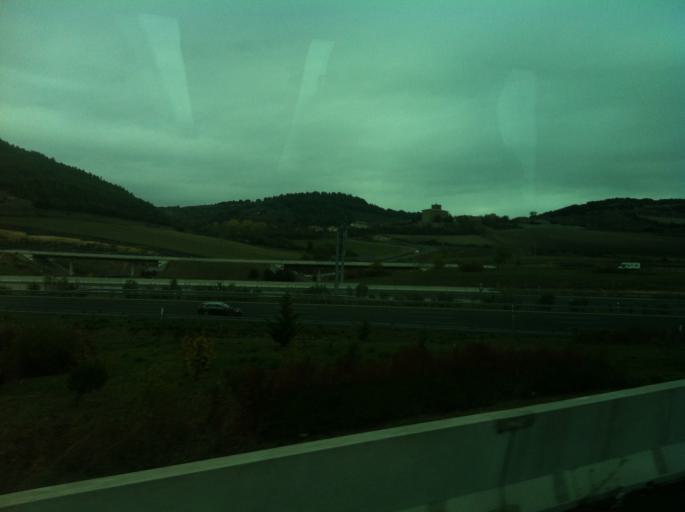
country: ES
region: Basque Country
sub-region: Provincia de Alava
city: Arminon
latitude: 42.7259
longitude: -2.8706
